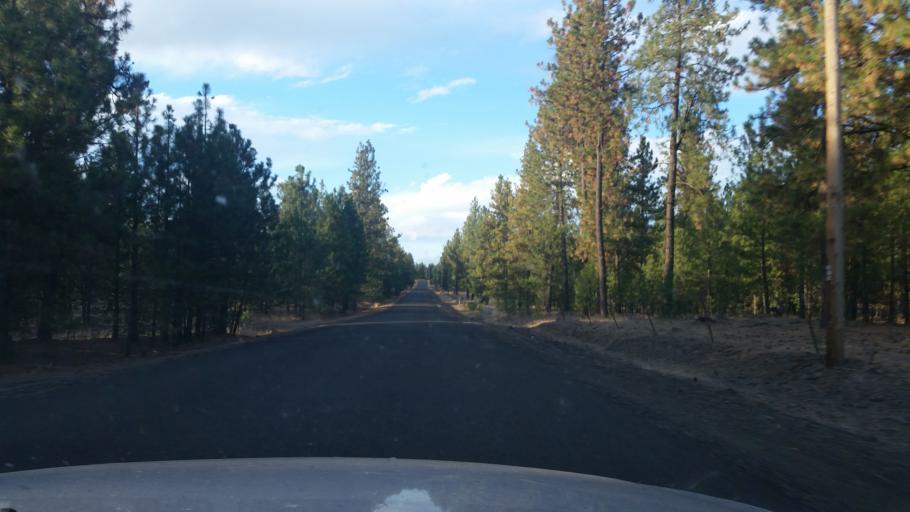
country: US
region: Washington
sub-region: Spokane County
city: Medical Lake
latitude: 47.4419
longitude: -117.7897
